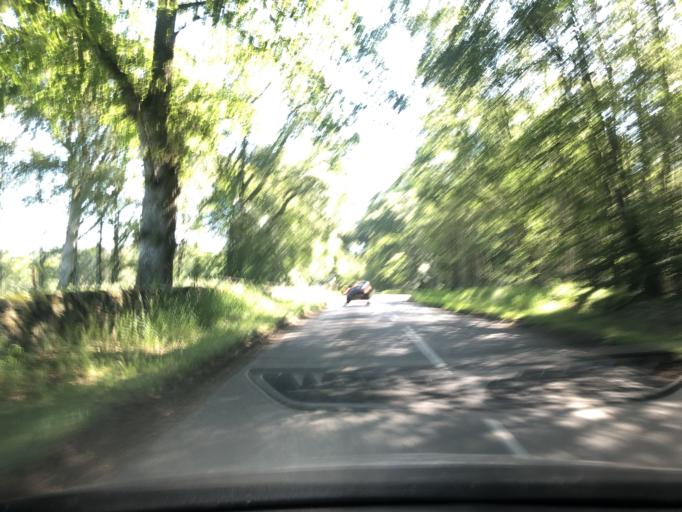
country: GB
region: Scotland
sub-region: Angus
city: Brechin
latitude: 56.8294
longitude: -2.6489
